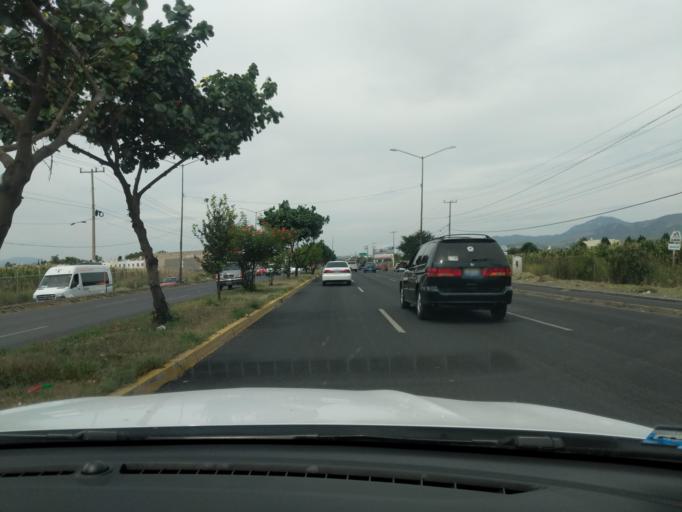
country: MX
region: Jalisco
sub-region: Zapopan
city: La Cuchilla (Extramuros de Tesistan)
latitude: 20.7794
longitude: -103.4599
